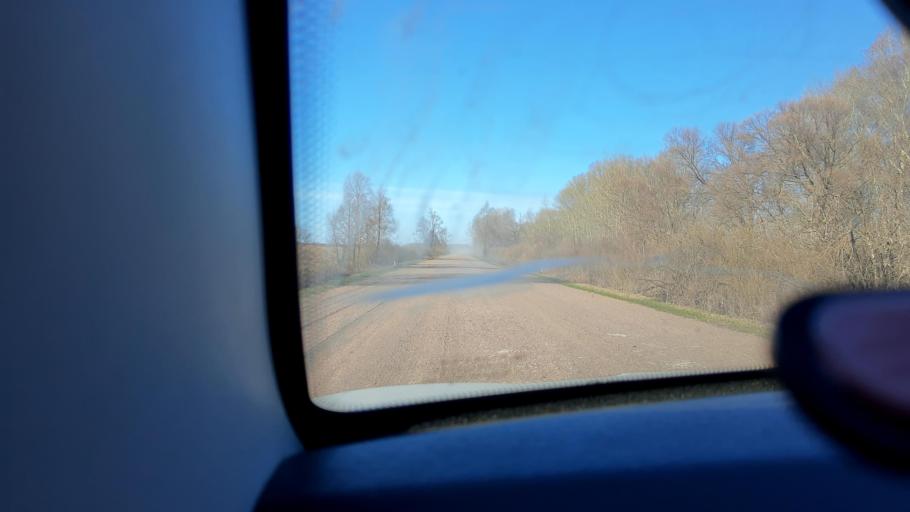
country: RU
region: Bashkortostan
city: Asanovo
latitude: 54.8712
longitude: 55.4668
